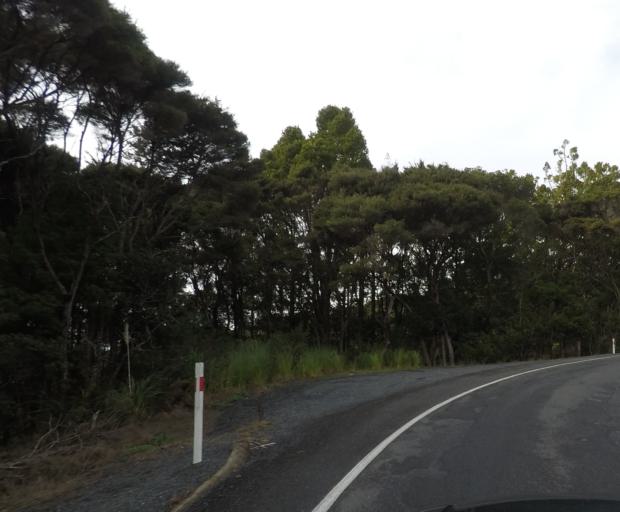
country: NZ
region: Northland
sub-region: Whangarei
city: Ruakaka
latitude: -36.0602
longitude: 174.5686
